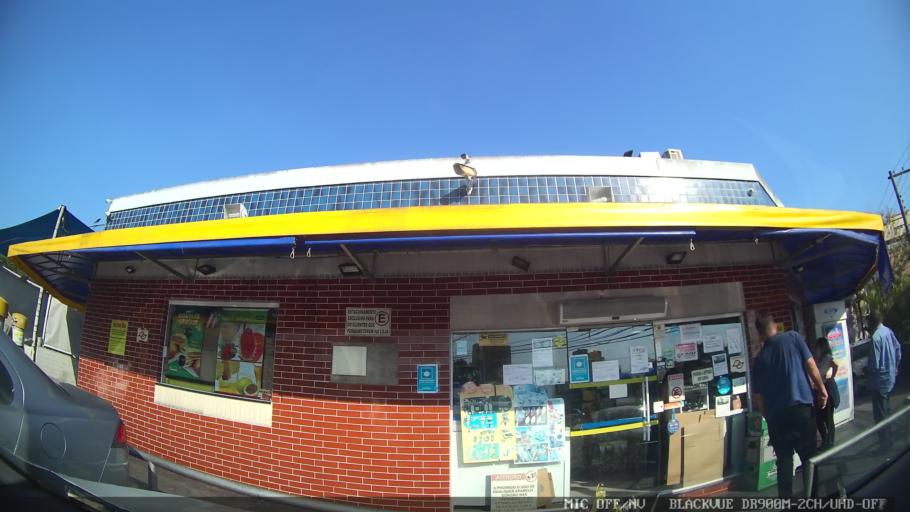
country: BR
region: Sao Paulo
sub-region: Osasco
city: Osasco
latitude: -23.5186
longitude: -46.7284
